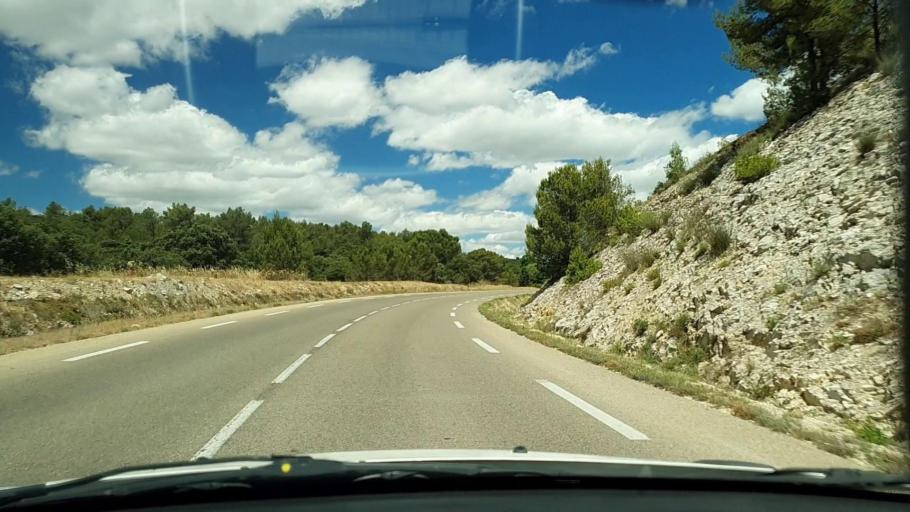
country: FR
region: Languedoc-Roussillon
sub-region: Departement du Gard
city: Poulx
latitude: 43.8882
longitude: 4.4169
